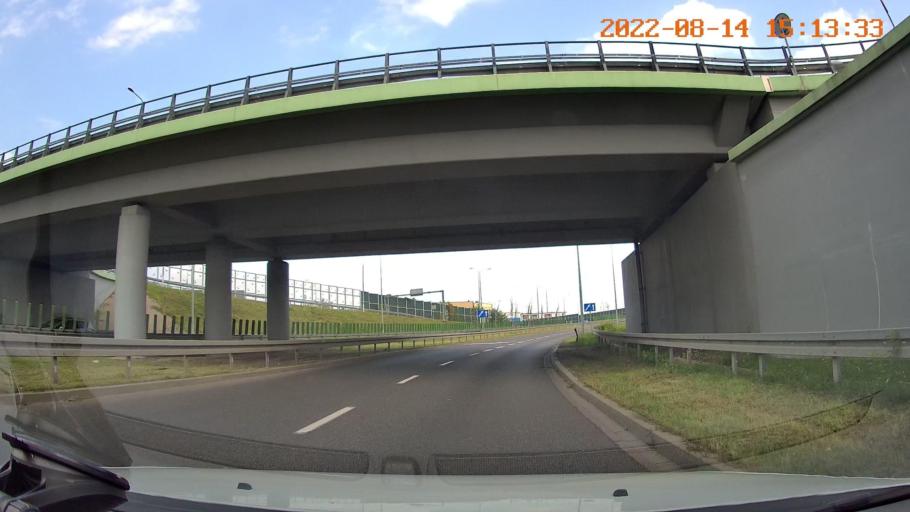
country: PL
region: Swietokrzyskie
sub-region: Powiat kielecki
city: Kielce
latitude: 50.8787
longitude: 20.6217
